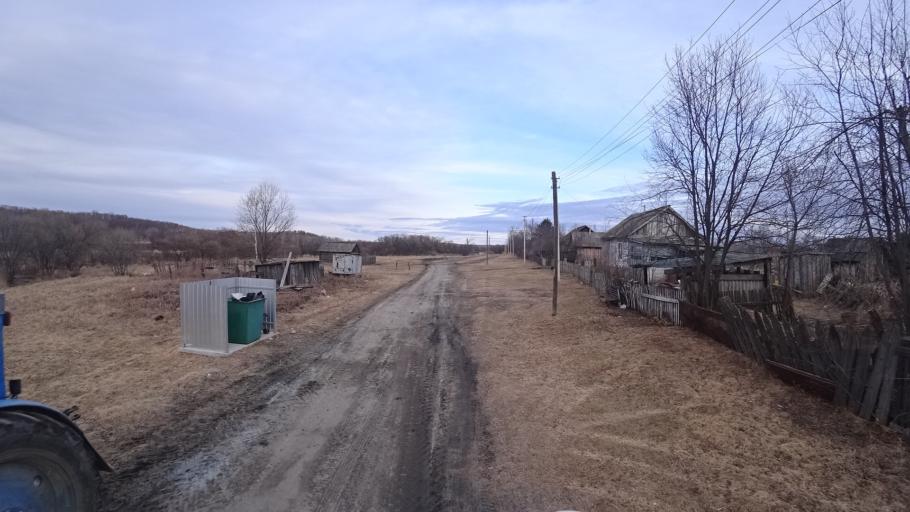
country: RU
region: Amur
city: Bureya
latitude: 50.0219
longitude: 129.7689
